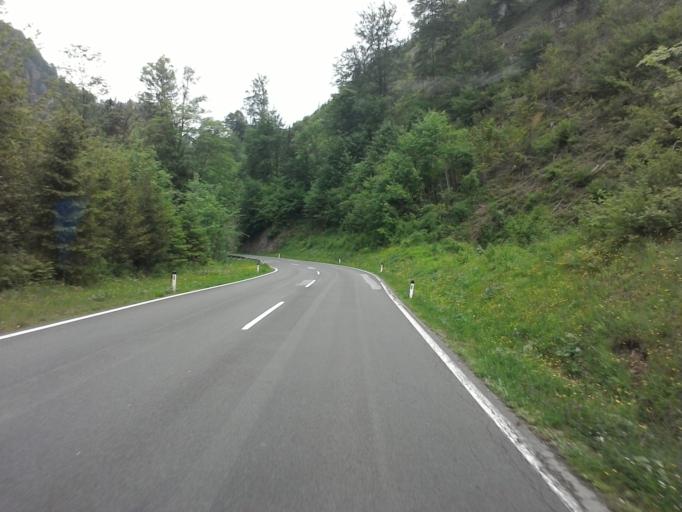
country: AT
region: Styria
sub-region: Politischer Bezirk Liezen
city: Altenmarkt bei Sankt Gallen
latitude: 47.7608
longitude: 14.6470
